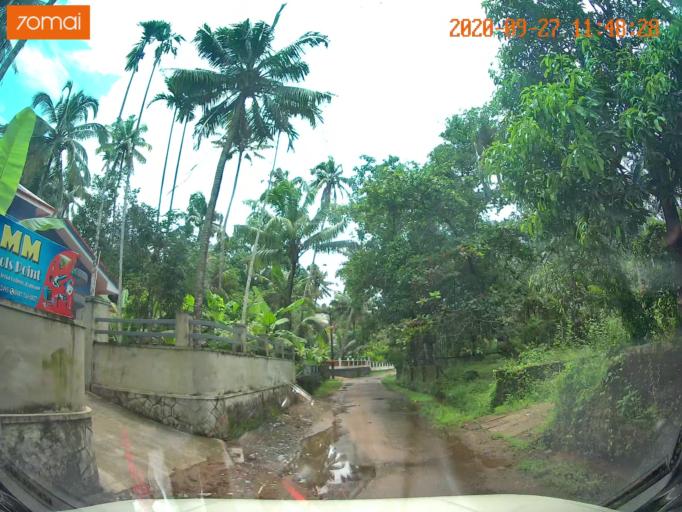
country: IN
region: Kerala
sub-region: Thrissur District
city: Thanniyam
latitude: 10.4725
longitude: 76.1124
